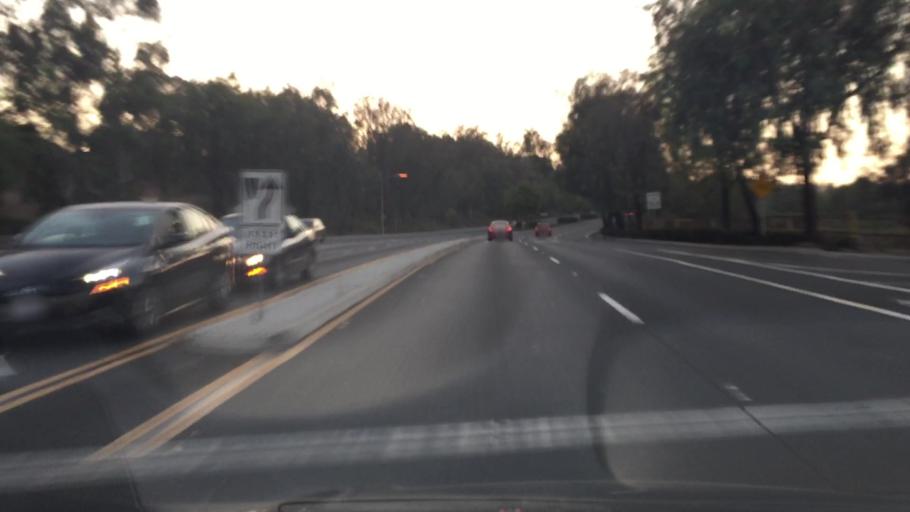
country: US
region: California
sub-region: San Diego County
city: Poway
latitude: 32.9837
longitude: -117.0620
